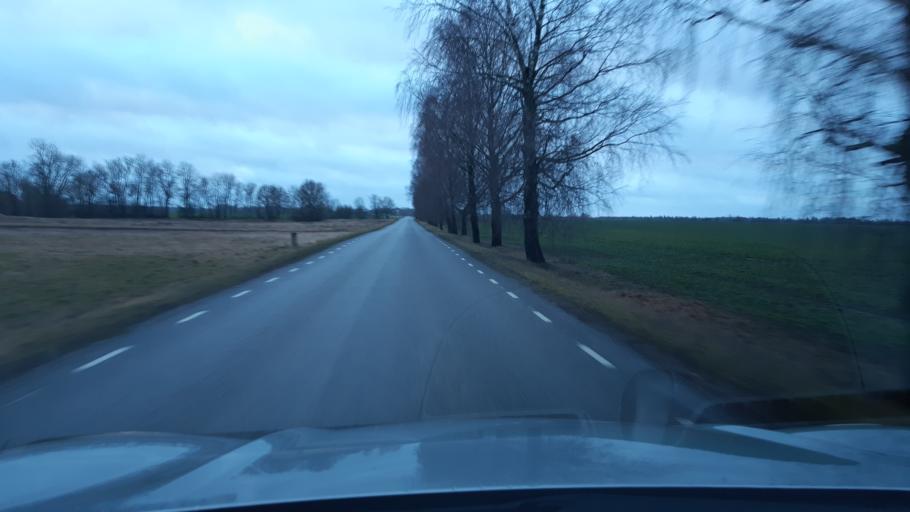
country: EE
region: Raplamaa
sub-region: Rapla vald
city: Rapla
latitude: 59.0534
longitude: 24.6845
